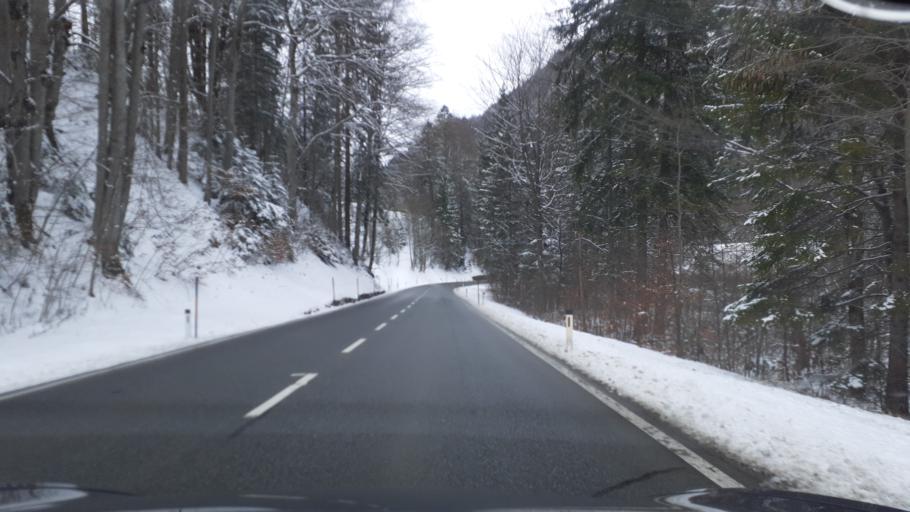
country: AT
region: Vorarlberg
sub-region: Politischer Bezirk Bludenz
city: Dalaas
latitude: 47.1258
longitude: 9.9815
